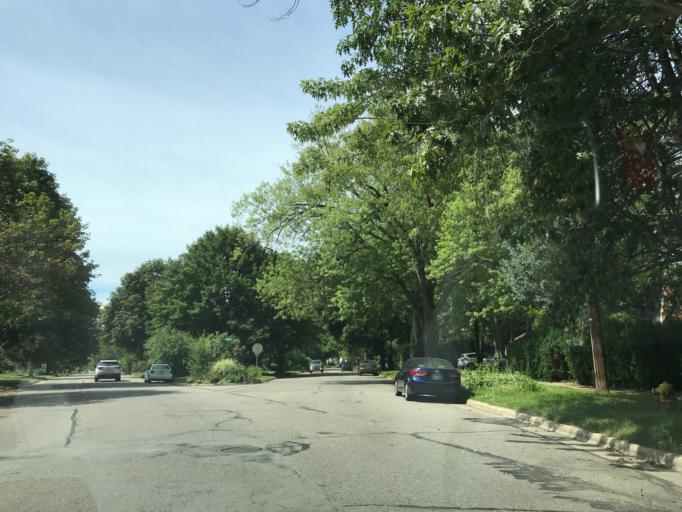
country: US
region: Michigan
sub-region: Washtenaw County
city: Ypsilanti
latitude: 42.2410
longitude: -83.6306
